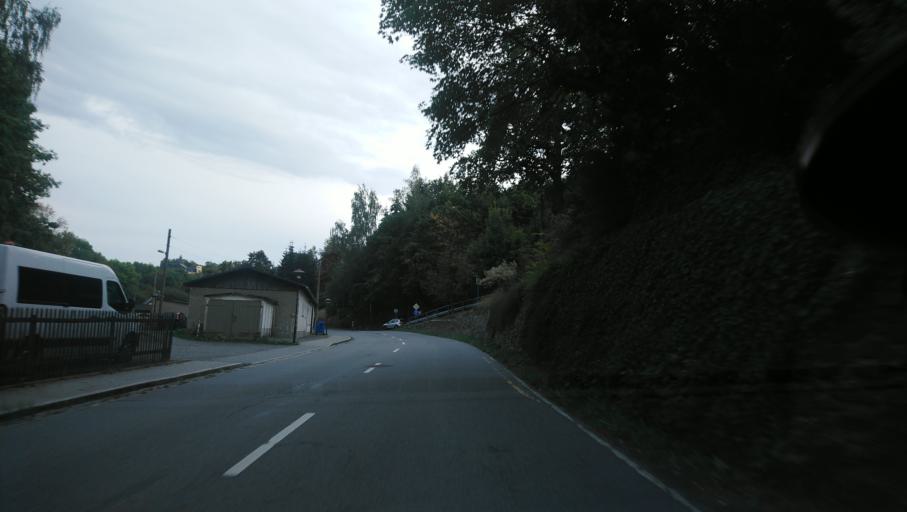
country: DE
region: Saxony
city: Annaberg-Buchholz
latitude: 50.5798
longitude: 12.9965
